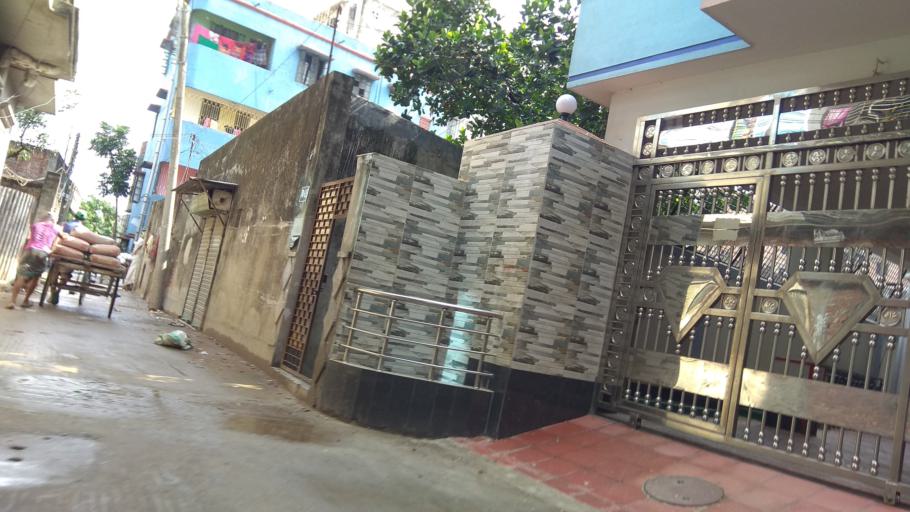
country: BD
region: Dhaka
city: Azimpur
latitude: 23.8088
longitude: 90.3811
